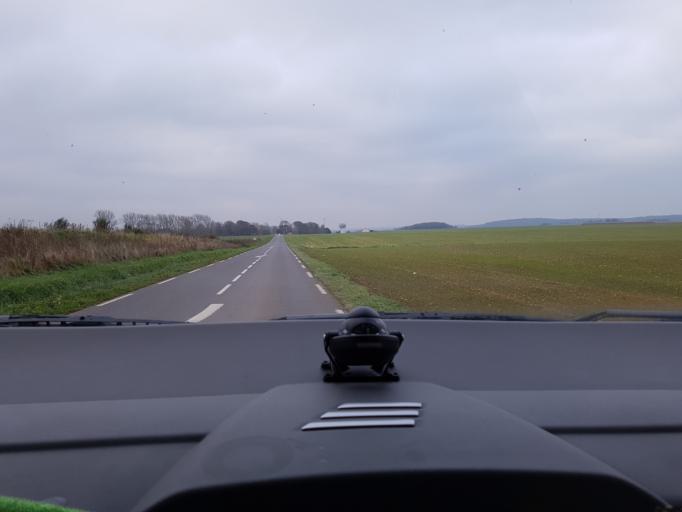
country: FR
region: Haute-Normandie
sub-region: Departement de la Seine-Maritime
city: Le Treport
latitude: 50.0349
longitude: 1.3597
